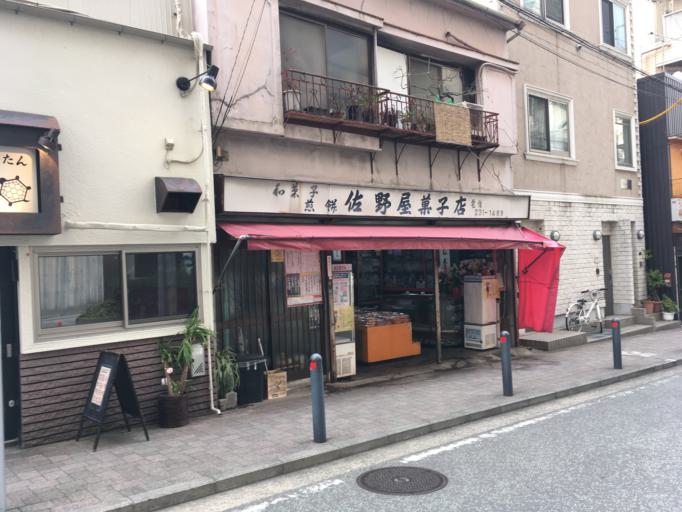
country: JP
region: Kanagawa
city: Yokohama
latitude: 35.4491
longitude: 139.6289
